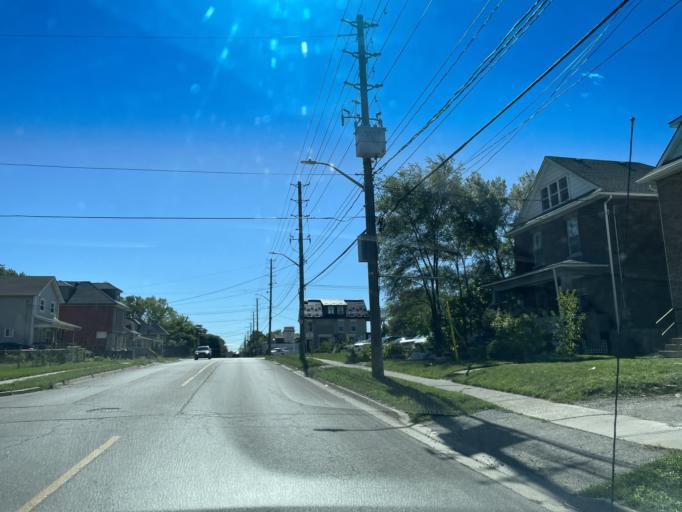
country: CA
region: Ontario
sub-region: Wellington County
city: Guelph
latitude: 43.5506
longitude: -80.2256
